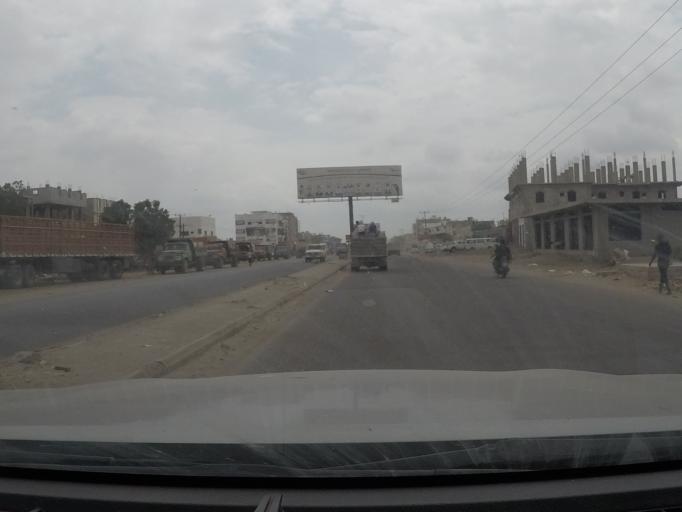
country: YE
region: Lahij
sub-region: Al  Hawtah
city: Lahij
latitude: 13.0087
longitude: 44.9177
